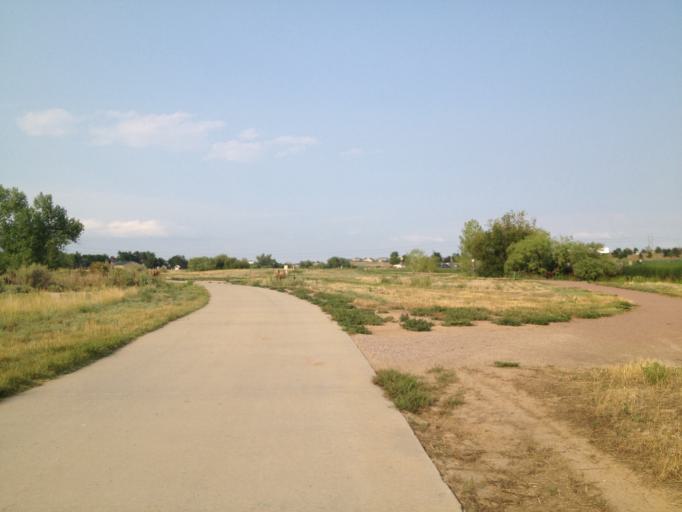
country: US
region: Colorado
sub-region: Broomfield County
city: Broomfield
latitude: 39.8894
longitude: -105.0621
